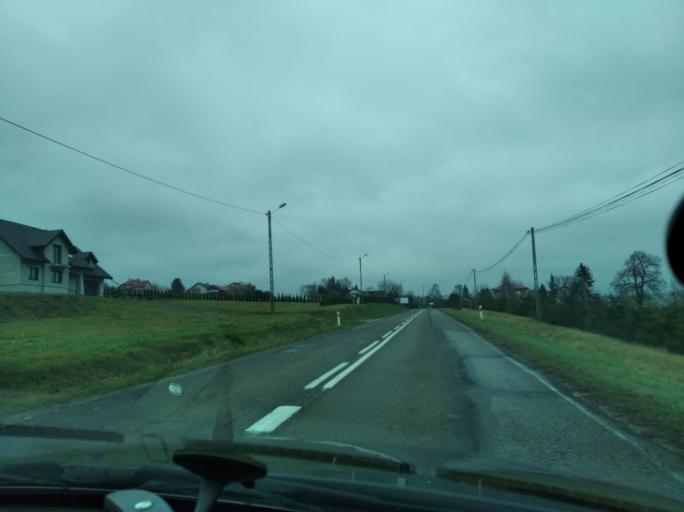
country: PL
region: Subcarpathian Voivodeship
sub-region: Powiat rzeszowski
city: Dynow
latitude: 49.8612
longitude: 22.2479
